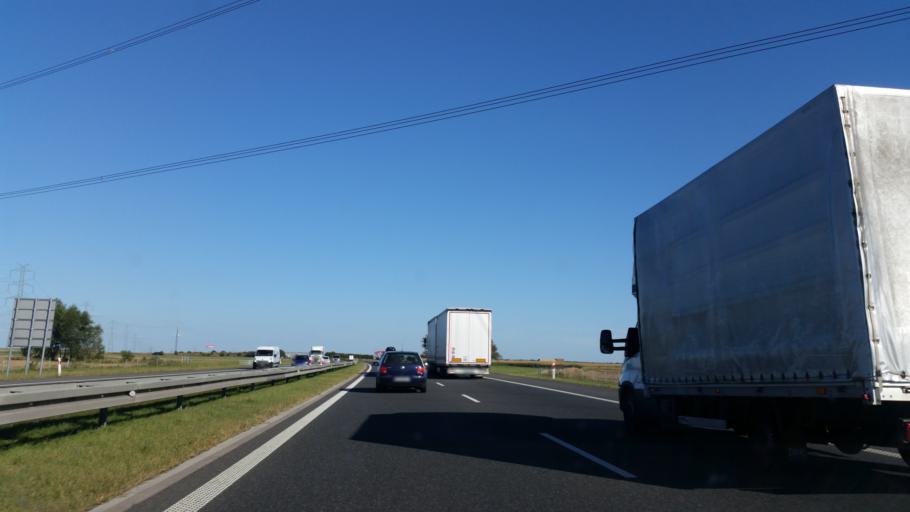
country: PL
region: Opole Voivodeship
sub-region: Powiat brzeski
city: Olszanka
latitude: 50.7415
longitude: 17.4598
